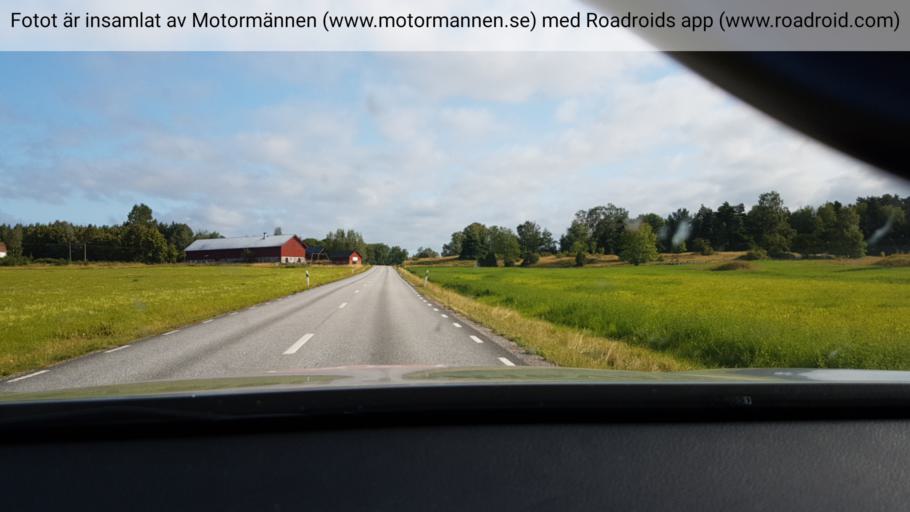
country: SE
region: Stockholm
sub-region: Norrtalje Kommun
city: Rimbo
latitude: 59.7009
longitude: 18.3726
